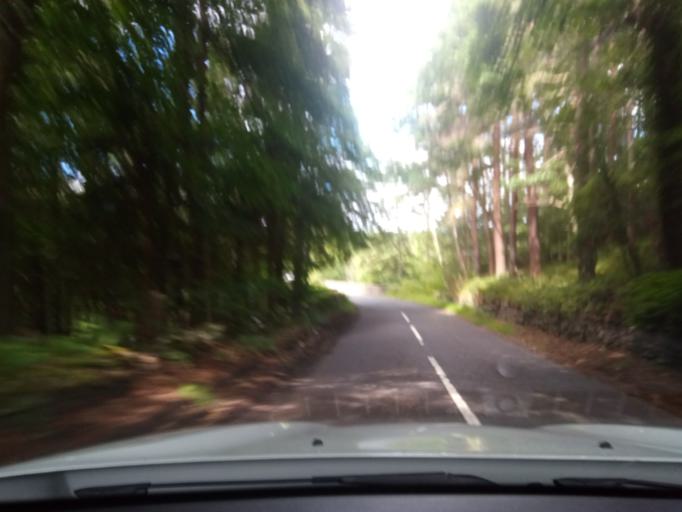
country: GB
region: Scotland
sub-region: The Scottish Borders
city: Selkirk
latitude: 55.5589
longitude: -2.9251
